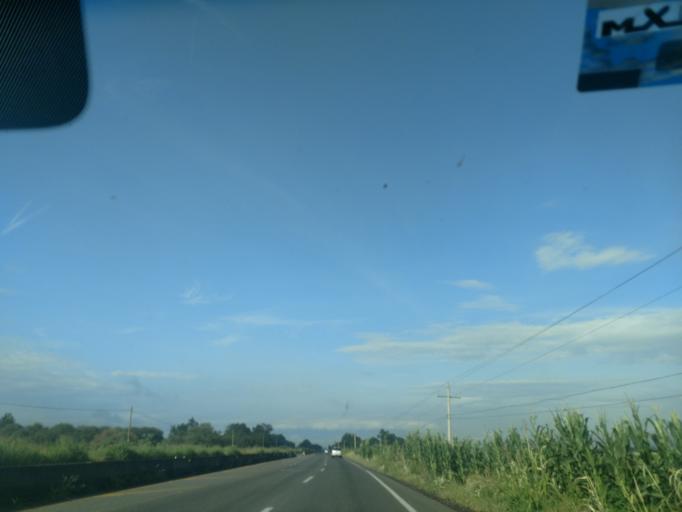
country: MX
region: Jalisco
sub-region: Ameca
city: Los Pocitos
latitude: 20.5523
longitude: -103.8949
